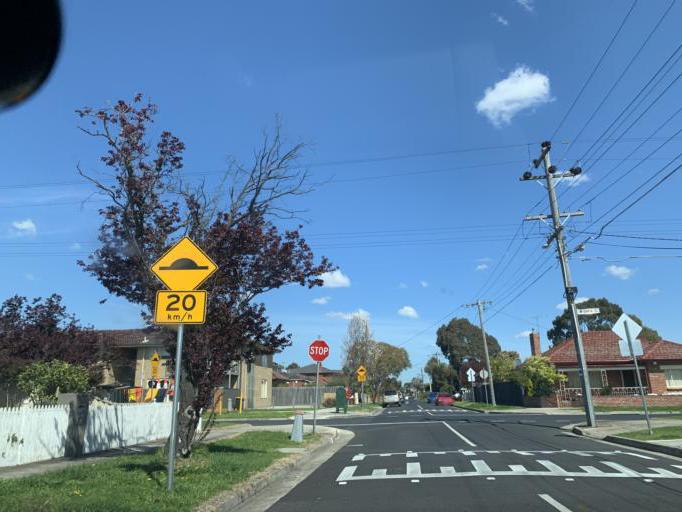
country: AU
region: Victoria
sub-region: Moreland
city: Pascoe Vale
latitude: -37.7342
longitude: 144.9353
